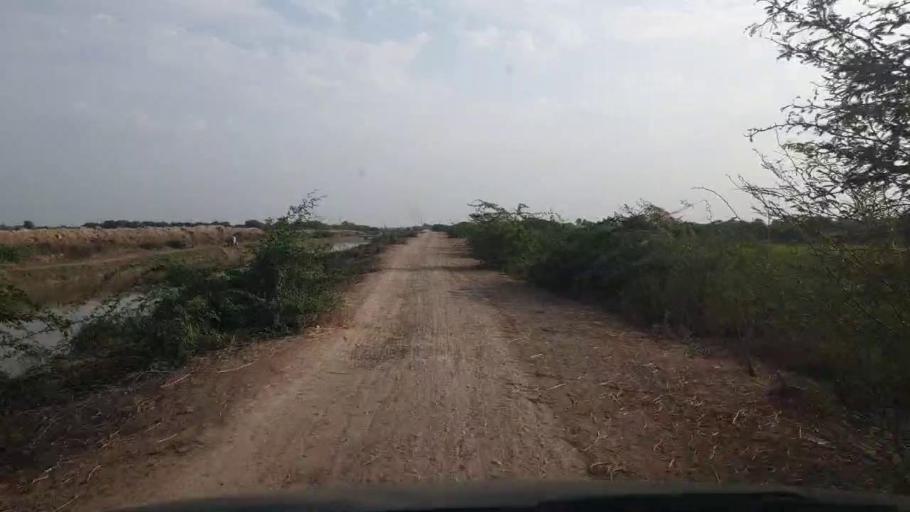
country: PK
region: Sindh
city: Badin
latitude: 24.5527
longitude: 68.6705
